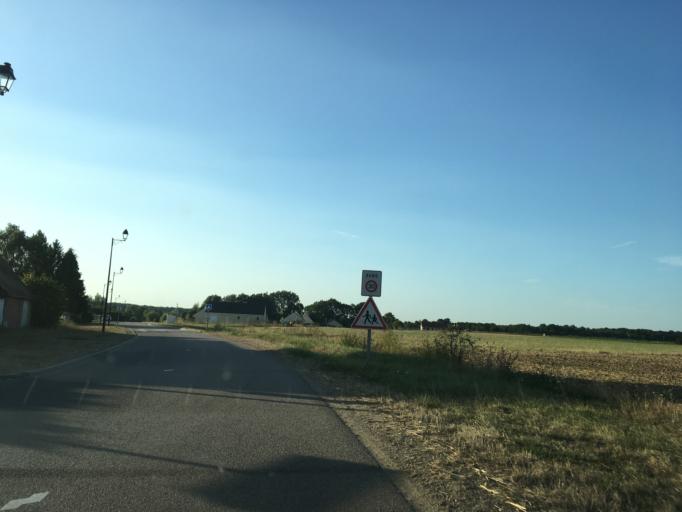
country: FR
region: Haute-Normandie
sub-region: Departement de l'Eure
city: Saint-Aubin-sur-Gaillon
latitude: 49.1341
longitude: 1.3053
